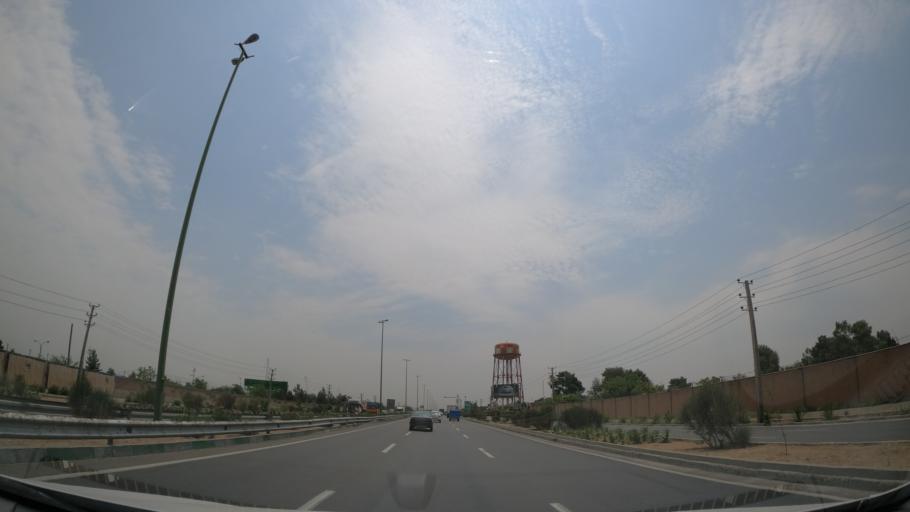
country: IR
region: Tehran
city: Shahr-e Qods
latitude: 35.6951
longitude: 51.2041
